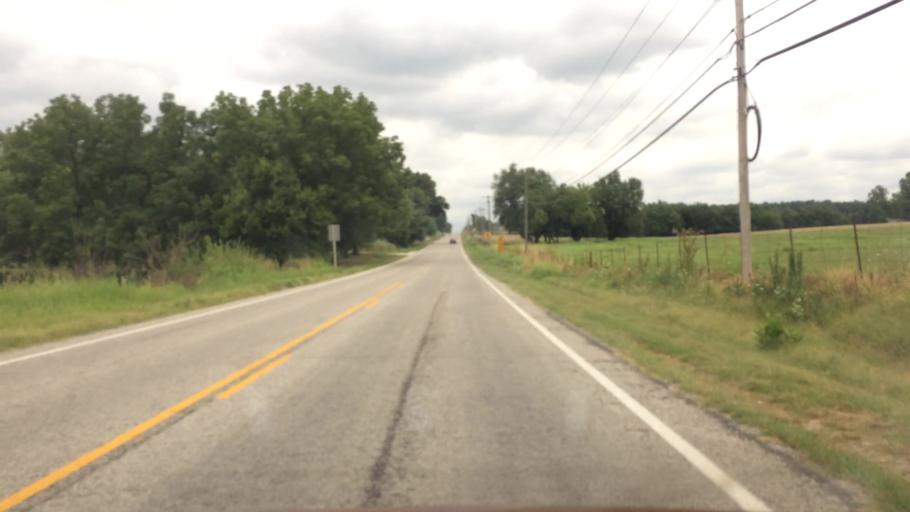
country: US
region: Missouri
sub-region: Greene County
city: Springfield
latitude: 37.2868
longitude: -93.2639
